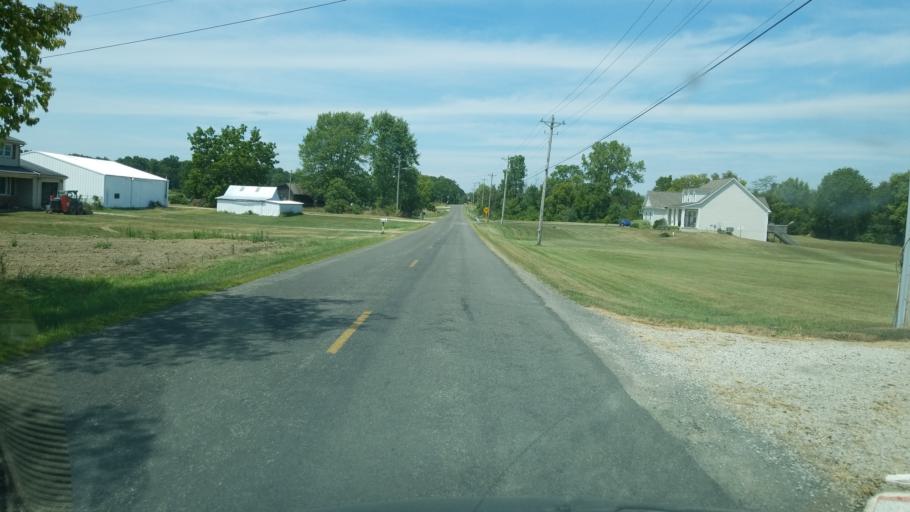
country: US
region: Ohio
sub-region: Union County
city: New California
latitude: 40.1453
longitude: -83.2569
